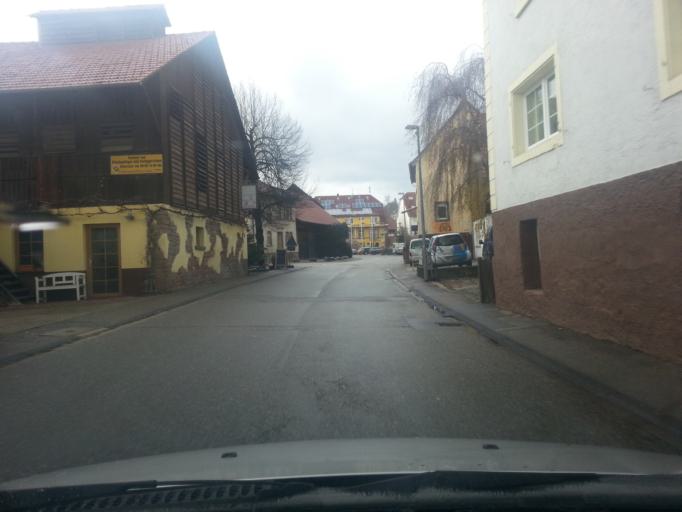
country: DE
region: Baden-Wuerttemberg
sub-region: Karlsruhe Region
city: Gaiberg
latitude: 49.3404
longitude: 8.7568
